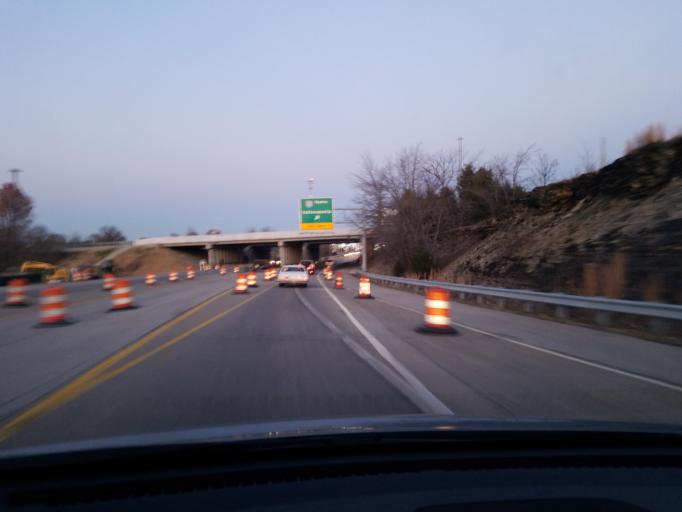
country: US
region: Indiana
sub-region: Clark County
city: Sellersburg
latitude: 38.3932
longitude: -85.7636
